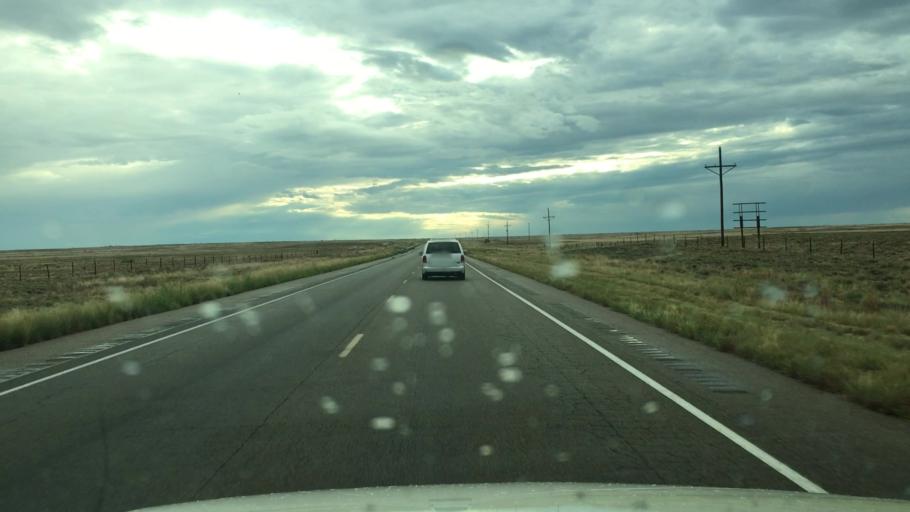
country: US
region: New Mexico
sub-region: Chaves County
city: Dexter
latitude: 33.4058
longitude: -104.3063
